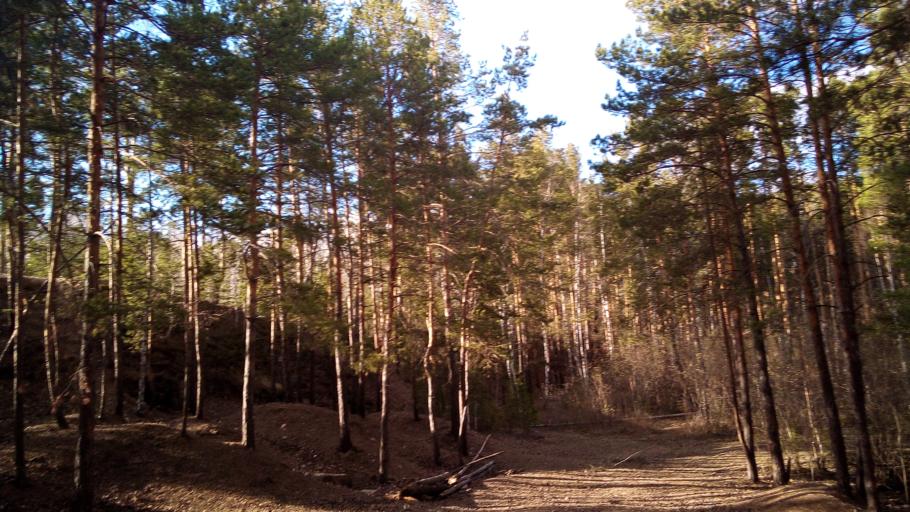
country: RU
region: Chelyabinsk
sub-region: Gorod Chelyabinsk
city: Chelyabinsk
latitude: 55.1646
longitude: 61.3250
